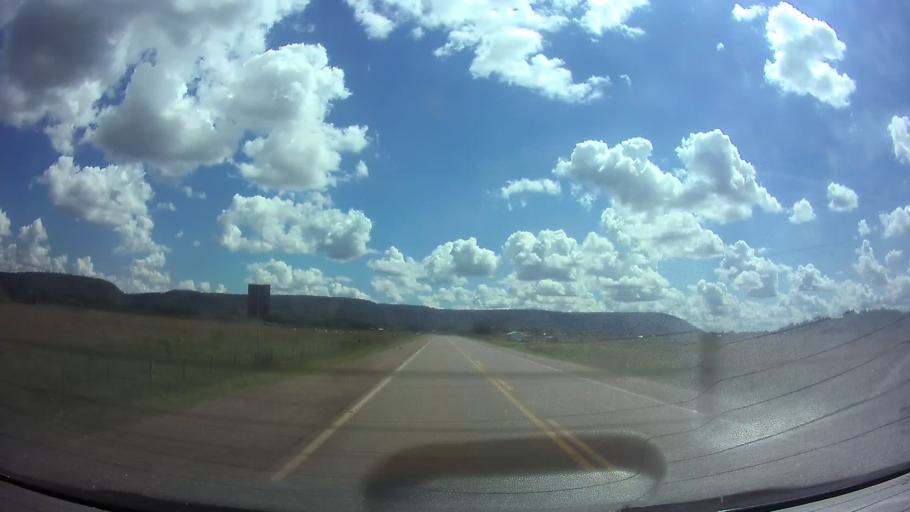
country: PY
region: Guaira
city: Itape
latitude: -25.9134
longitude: -56.6795
